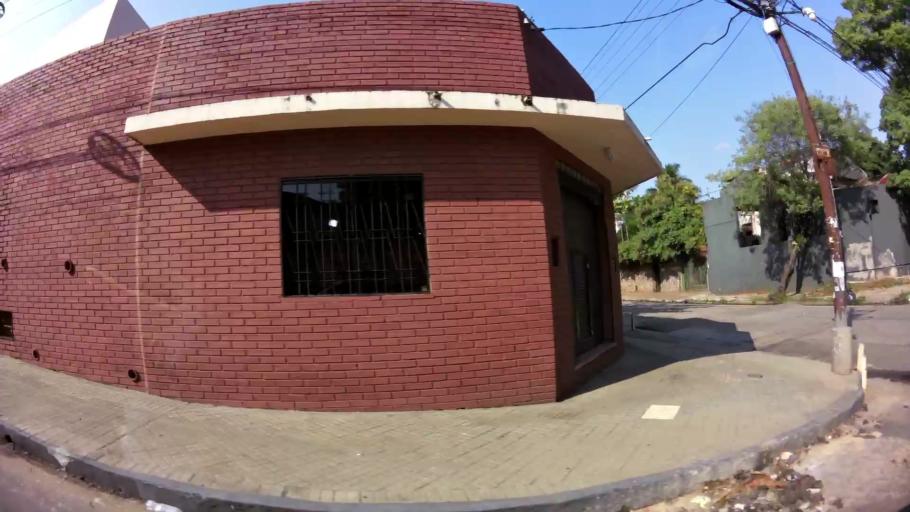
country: PY
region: Asuncion
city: Asuncion
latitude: -25.3073
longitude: -57.6227
